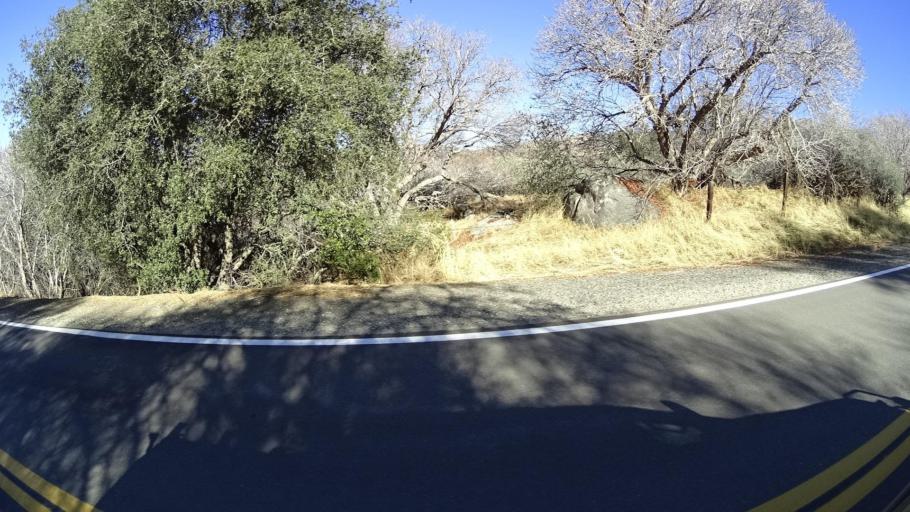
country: US
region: California
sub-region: Kern County
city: Alta Sierra
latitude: 35.7371
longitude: -118.6525
